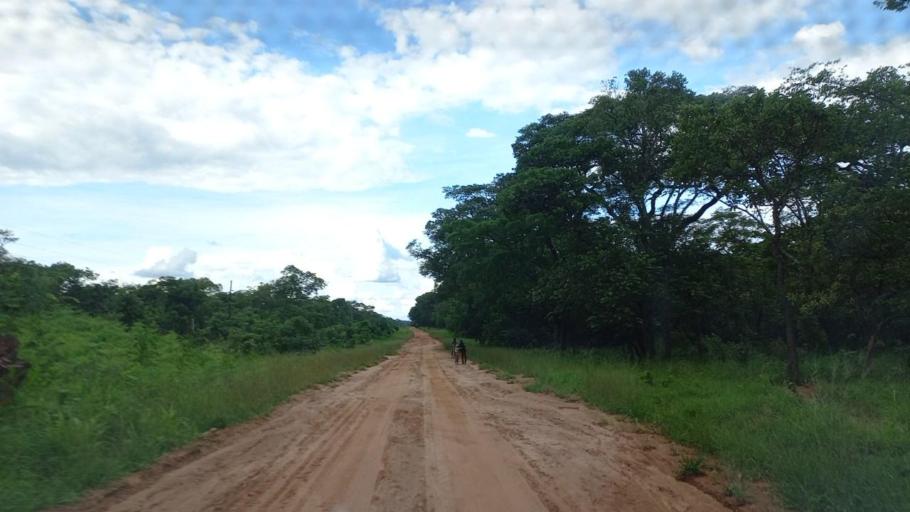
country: ZM
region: North-Western
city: Mwinilunga
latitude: -11.8086
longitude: 24.3684
